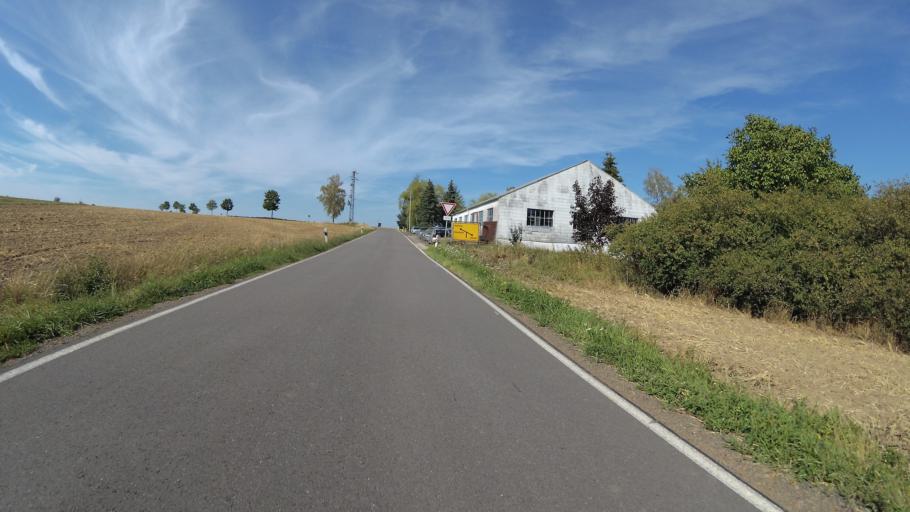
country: DE
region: Rheinland-Pfalz
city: Hornbach
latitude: 49.1740
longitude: 7.3018
